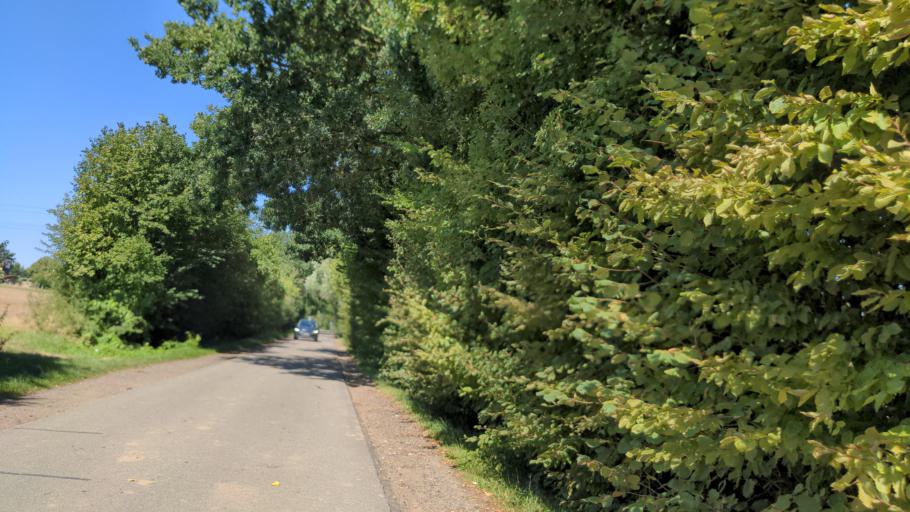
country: DE
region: Schleswig-Holstein
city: Grinau
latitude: 53.7746
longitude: 10.5551
